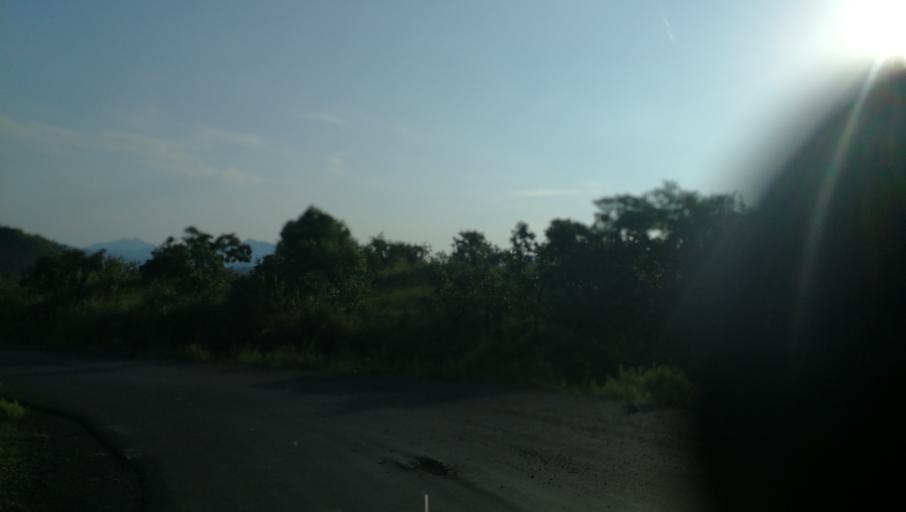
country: ET
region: Southern Nations, Nationalities, and People's Region
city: Areka
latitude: 6.8259
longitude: 37.3011
